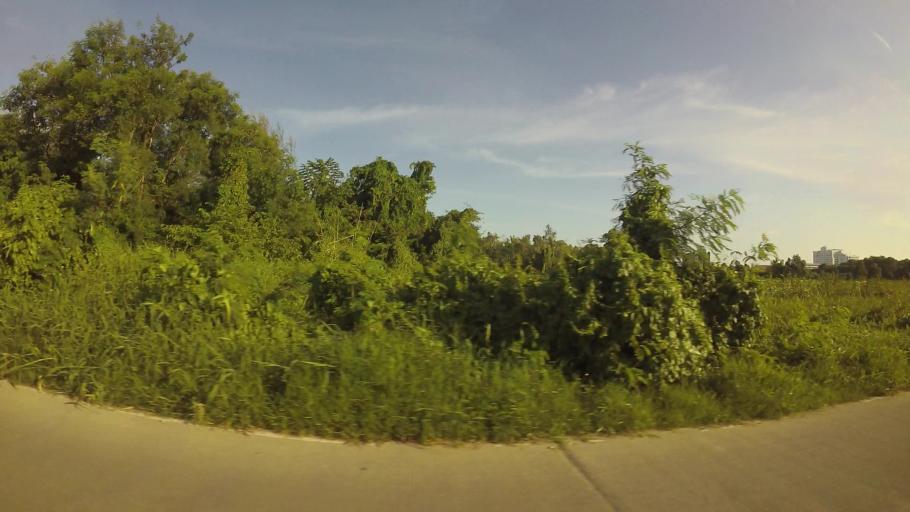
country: TH
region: Rayong
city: Rayong
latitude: 12.6883
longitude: 101.2838
